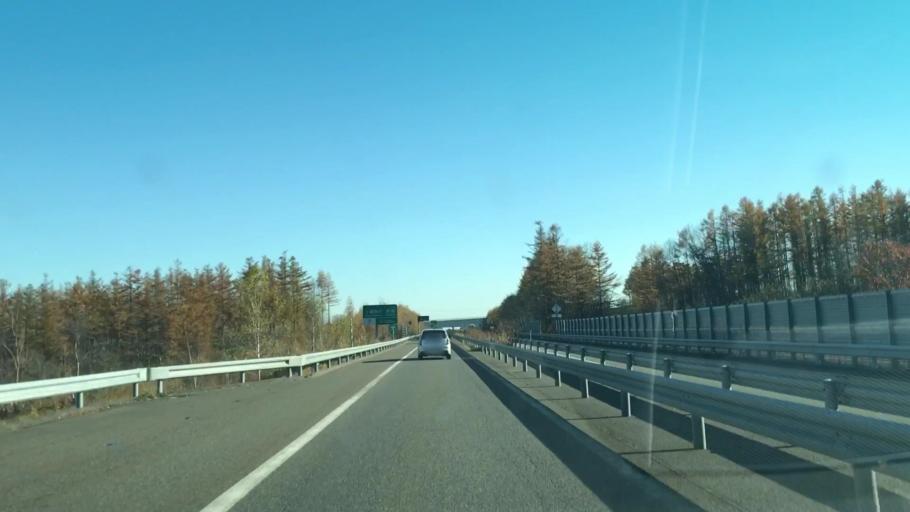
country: JP
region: Hokkaido
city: Otofuke
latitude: 43.0008
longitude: 142.8494
